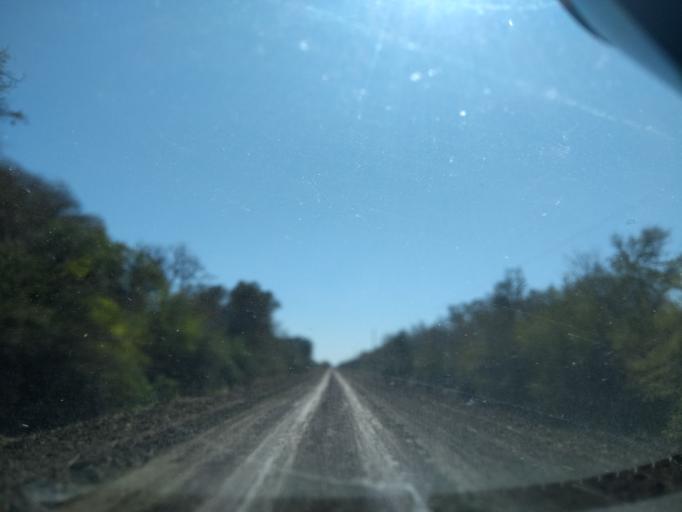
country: AR
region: Chaco
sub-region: Departamento de Quitilipi
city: Quitilipi
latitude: -26.7501
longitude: -60.2402
